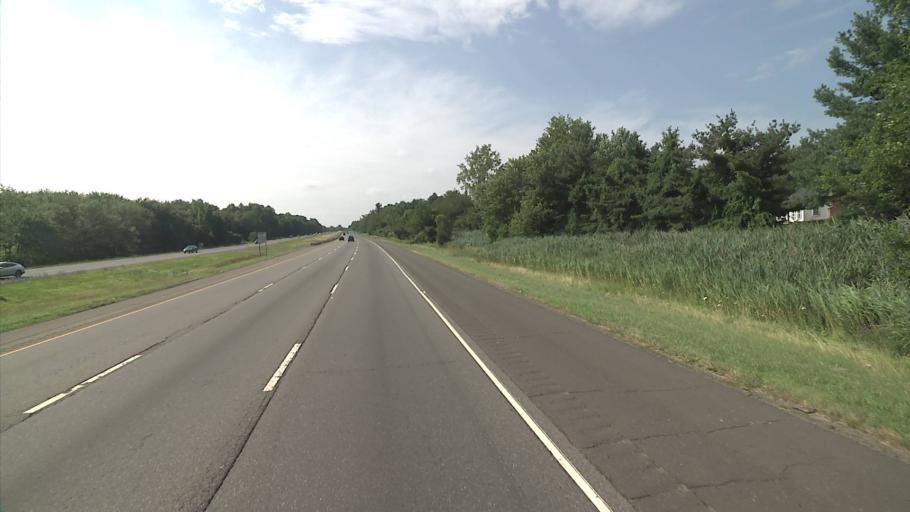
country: US
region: Connecticut
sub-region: New Haven County
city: Meriden
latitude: 41.5040
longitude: -72.7695
